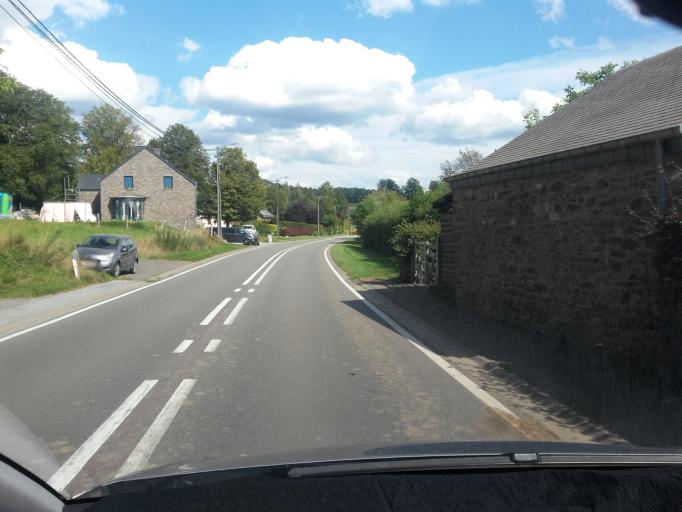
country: BE
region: Wallonia
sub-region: Province du Luxembourg
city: Saint-Hubert
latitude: 50.0289
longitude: 5.3486
